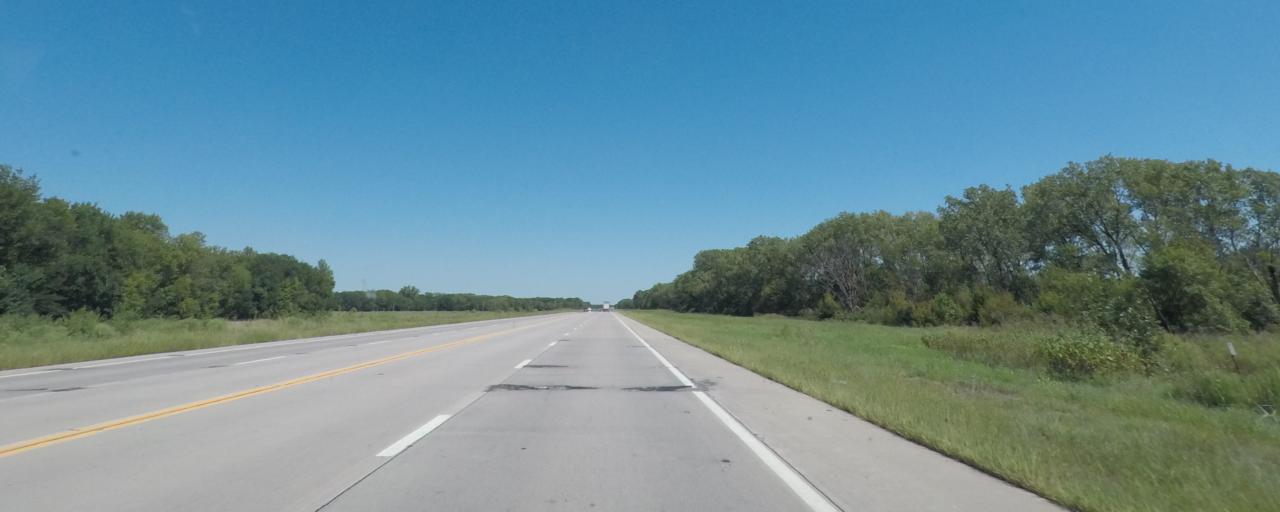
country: US
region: Kansas
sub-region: Lyon County
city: Emporia
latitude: 38.4067
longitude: -96.3414
